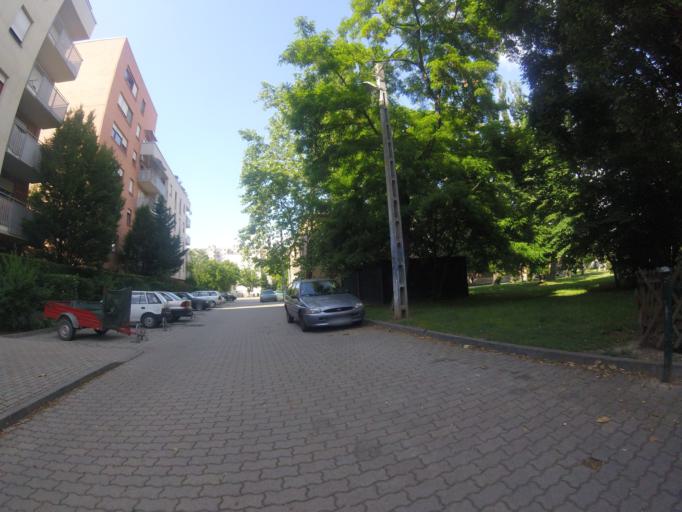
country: HU
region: Budapest
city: Budapest XIII. keruelet
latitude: 47.5468
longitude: 19.0759
